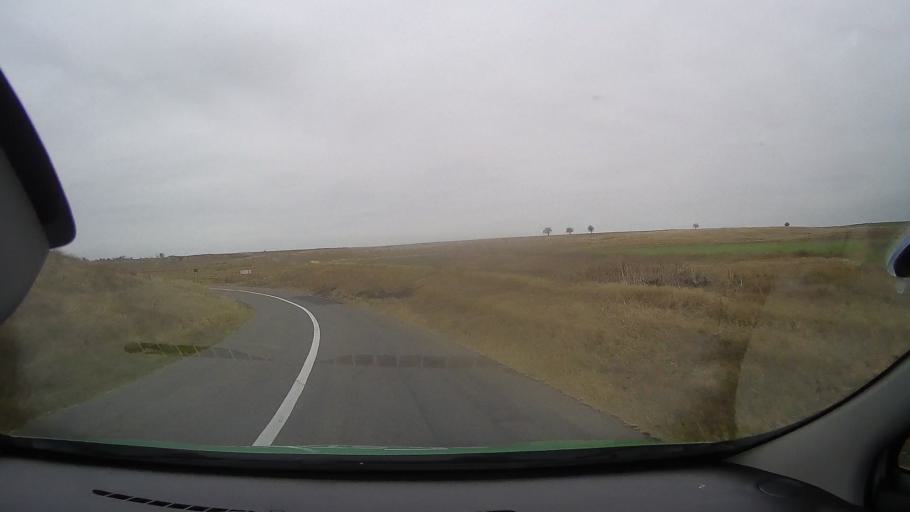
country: RO
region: Constanta
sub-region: Comuna Saraiu
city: Saraiu
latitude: 44.7271
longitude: 28.1740
